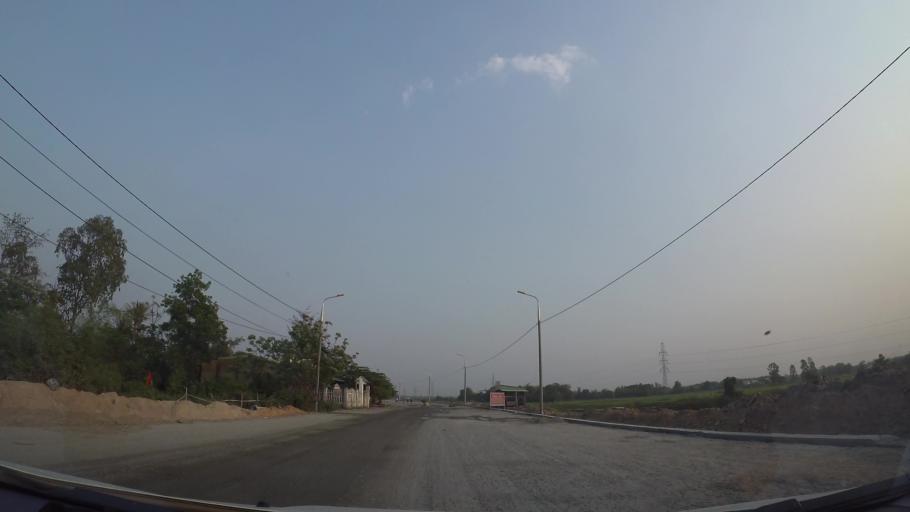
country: VN
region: Da Nang
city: Ngu Hanh Son
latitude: 15.9587
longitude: 108.2333
